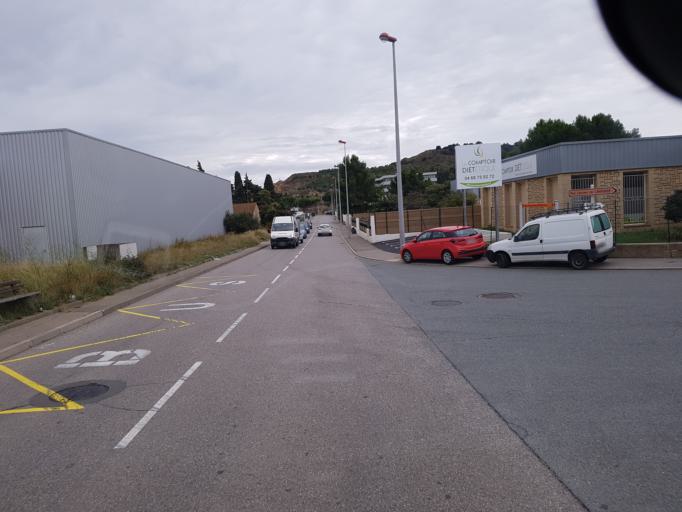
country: FR
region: Languedoc-Roussillon
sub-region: Departement de l'Aude
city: Narbonne
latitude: 43.1604
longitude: 2.9791
